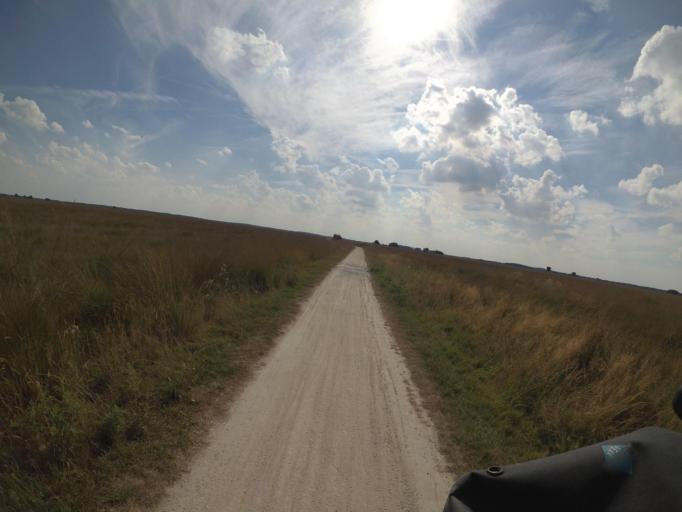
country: NL
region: Drenthe
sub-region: Gemeente Westerveld
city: Dwingeloo
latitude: 52.8088
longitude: 6.3980
